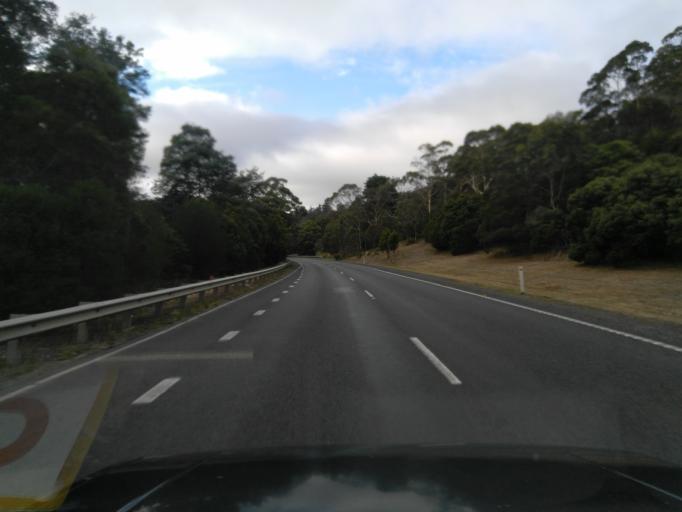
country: AU
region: Tasmania
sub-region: Hobart
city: Dynnyrne
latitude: -42.9261
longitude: 147.3051
